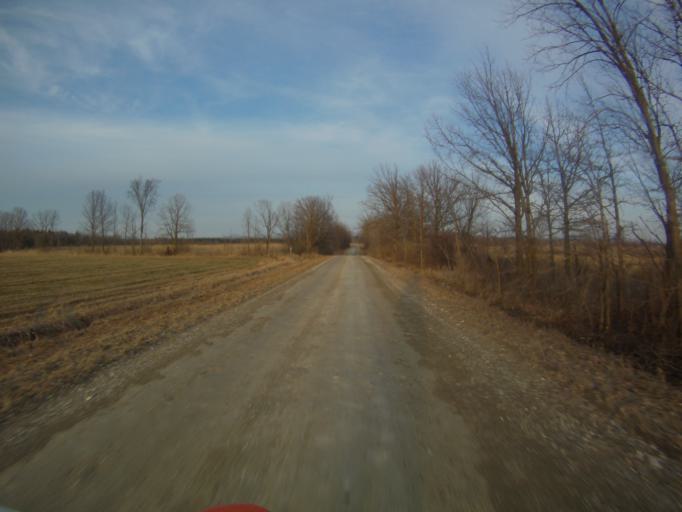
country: US
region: Vermont
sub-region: Addison County
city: Vergennes
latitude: 44.1299
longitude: -73.3198
